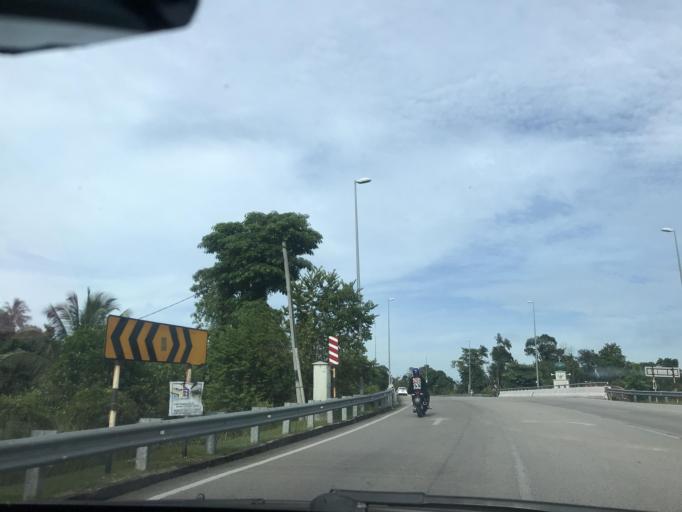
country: MY
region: Kelantan
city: Kota Bharu
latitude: 6.1387
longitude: 102.2051
